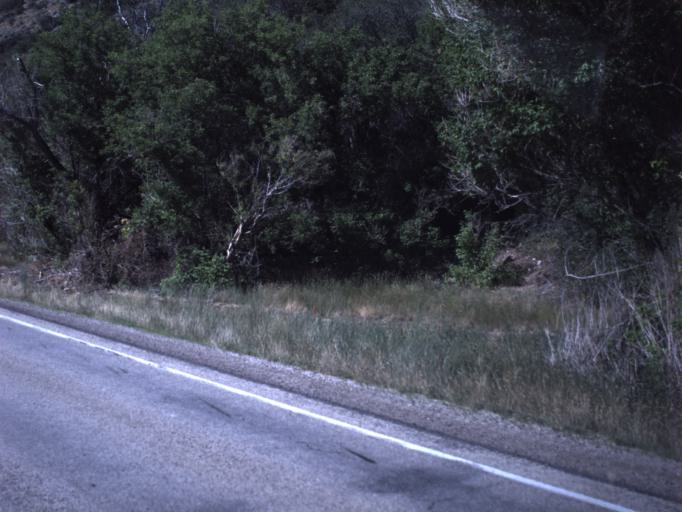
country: US
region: Utah
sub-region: Wasatch County
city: Heber
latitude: 40.4038
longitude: -111.3091
